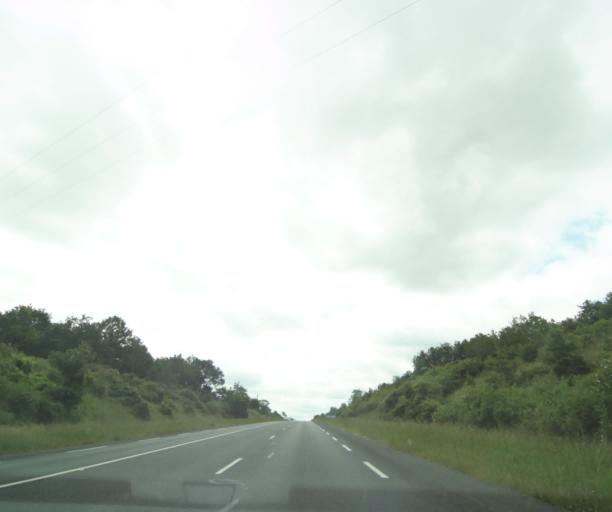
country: FR
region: Poitou-Charentes
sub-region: Departement des Deux-Sevres
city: Saint-Varent
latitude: 46.9114
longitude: -0.1943
